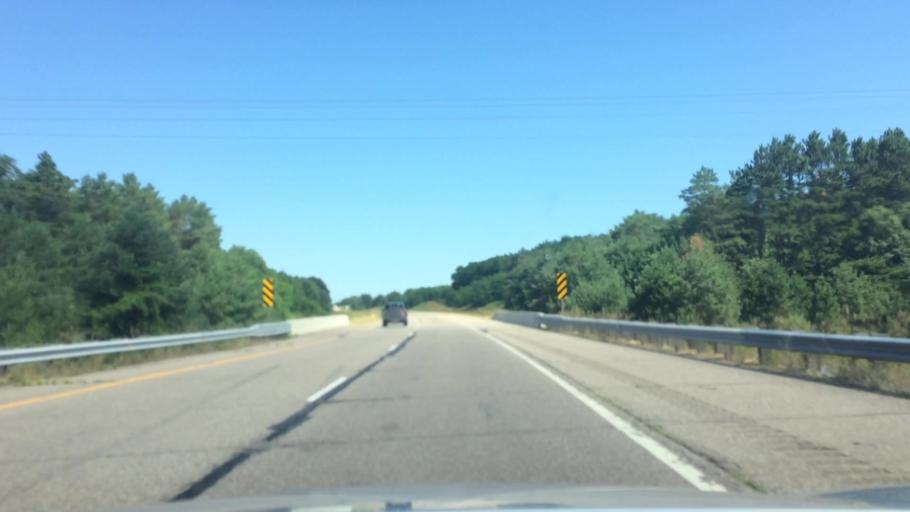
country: US
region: Wisconsin
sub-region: Marquette County
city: Westfield
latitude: 44.0823
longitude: -89.5322
